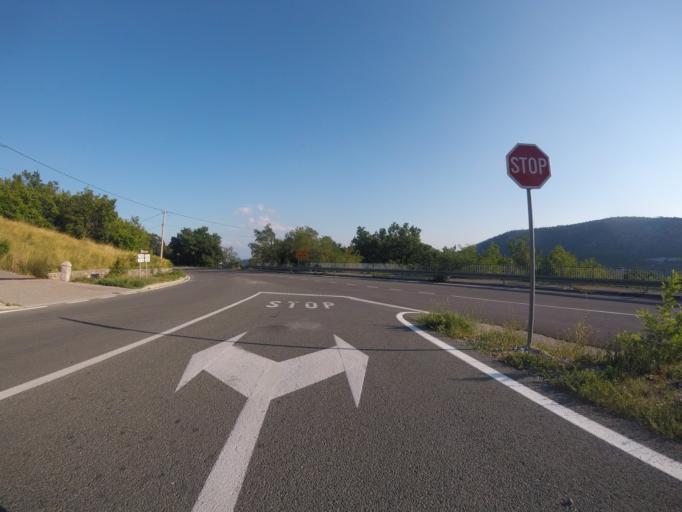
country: HR
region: Primorsko-Goranska
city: Bribir
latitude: 45.1666
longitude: 14.7531
